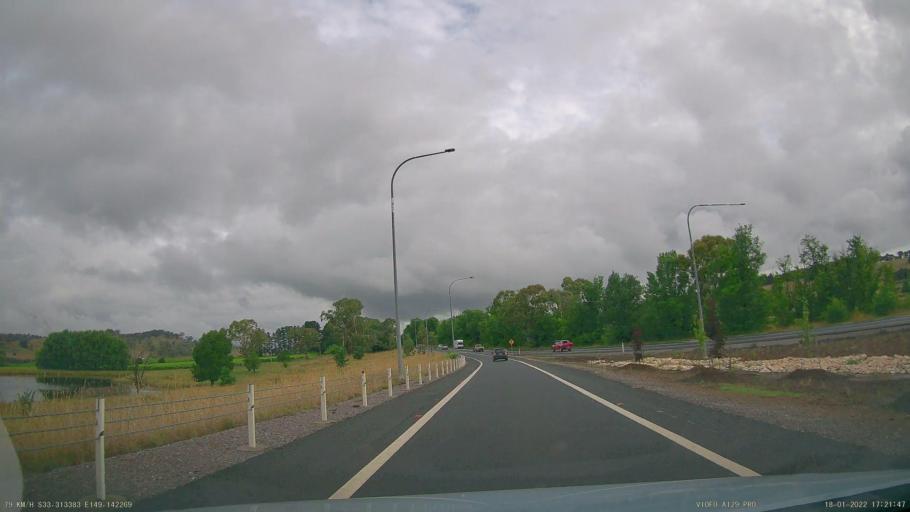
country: AU
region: New South Wales
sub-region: Orange Municipality
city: Orange
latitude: -33.3136
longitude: 149.1423
